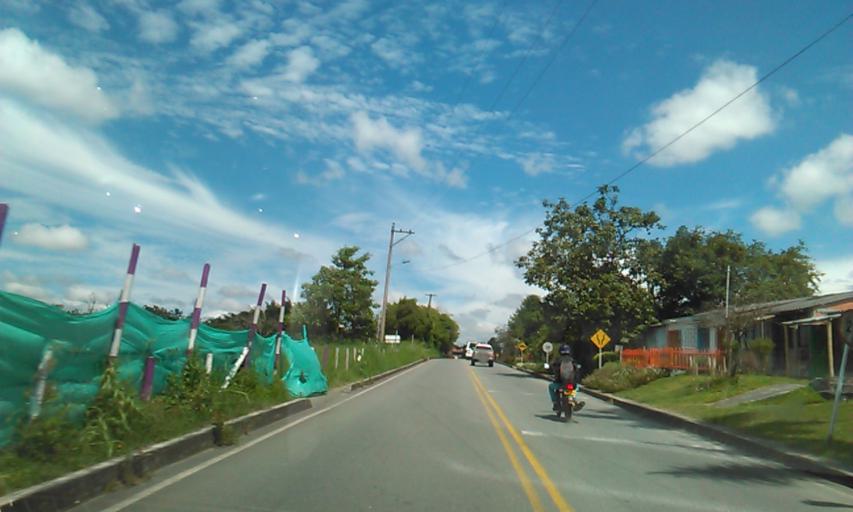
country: CO
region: Quindio
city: Cordoba
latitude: 4.4311
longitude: -75.7179
